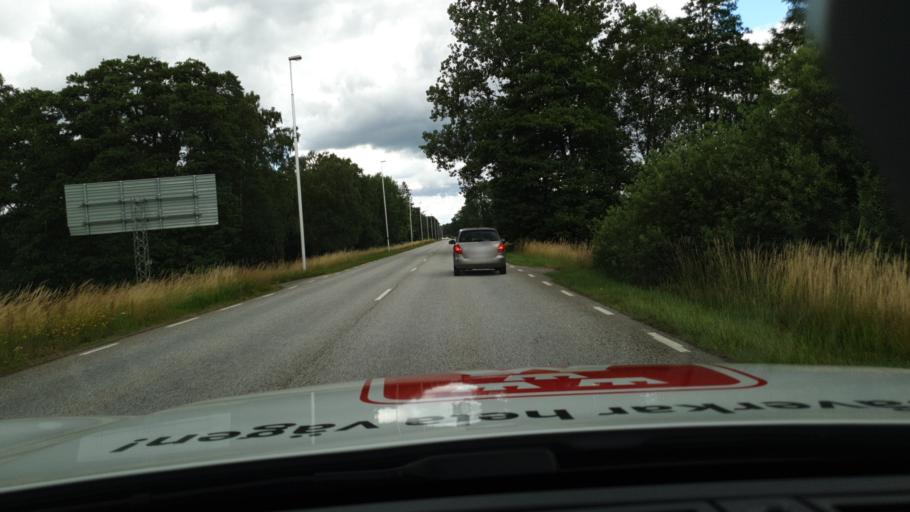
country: SE
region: Skane
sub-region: Hassleholms Kommun
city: Tormestorp
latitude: 56.1215
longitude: 13.7366
